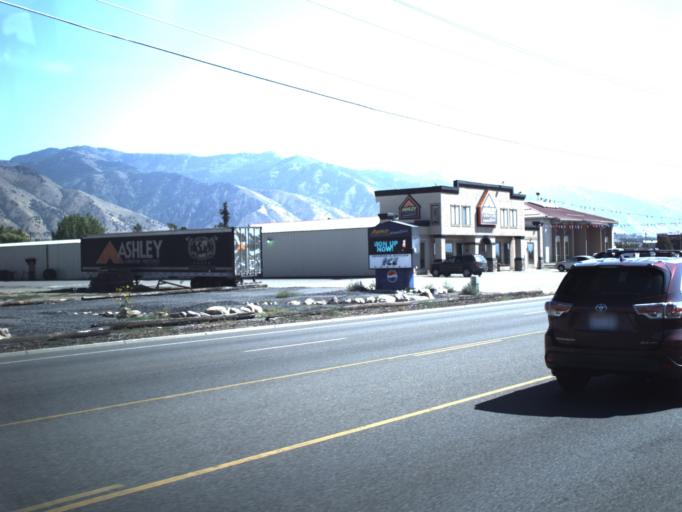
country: US
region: Utah
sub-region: Cache County
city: Hyde Park
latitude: 41.7815
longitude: -111.8340
